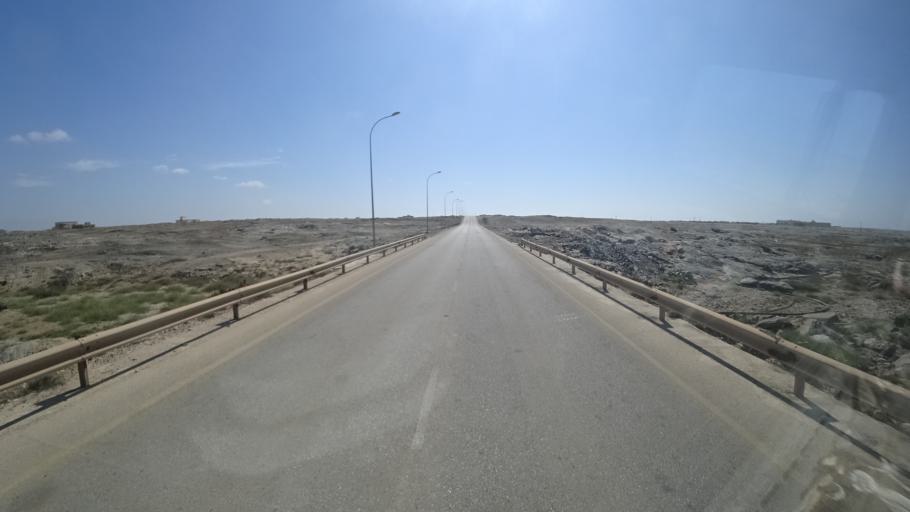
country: OM
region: Zufar
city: Salalah
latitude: 16.9685
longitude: 54.7302
